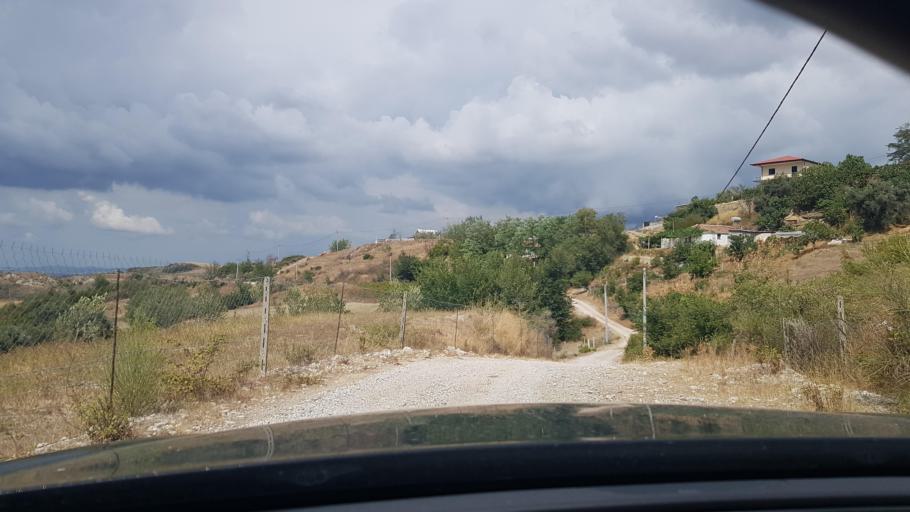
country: AL
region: Tirane
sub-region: Rrethi i Kavajes
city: Golem
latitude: 41.2860
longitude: 19.5478
